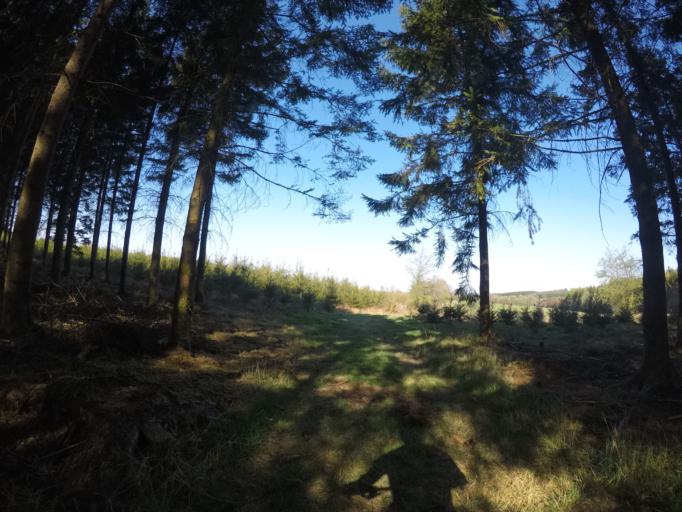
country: BE
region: Wallonia
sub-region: Province du Luxembourg
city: Leglise
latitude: 49.7987
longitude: 5.5802
